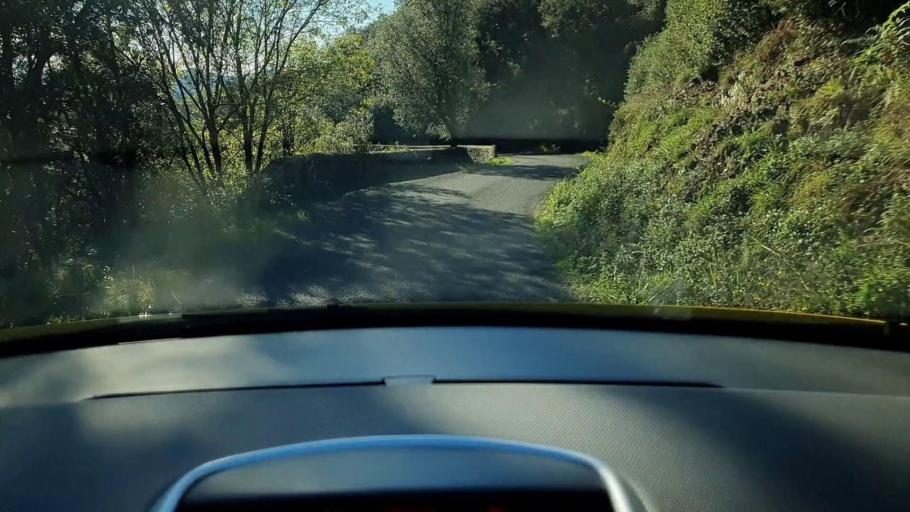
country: FR
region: Languedoc-Roussillon
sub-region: Departement du Gard
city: Sumene
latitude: 44.0340
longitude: 3.7034
